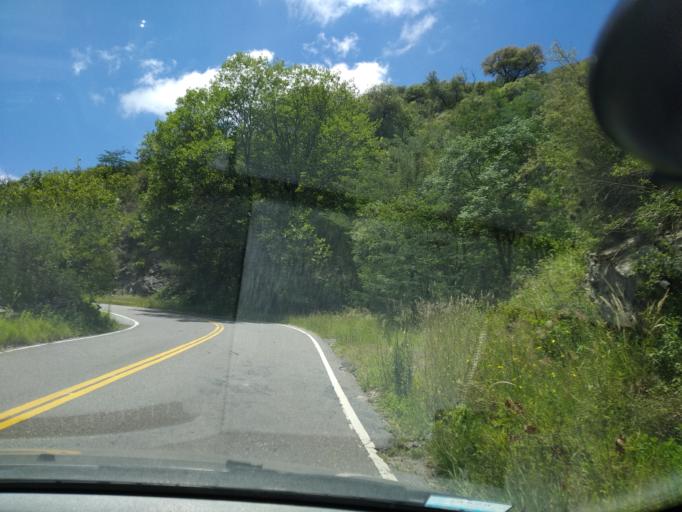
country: AR
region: Cordoba
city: Cuesta Blanca
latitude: -31.6045
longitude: -64.5524
